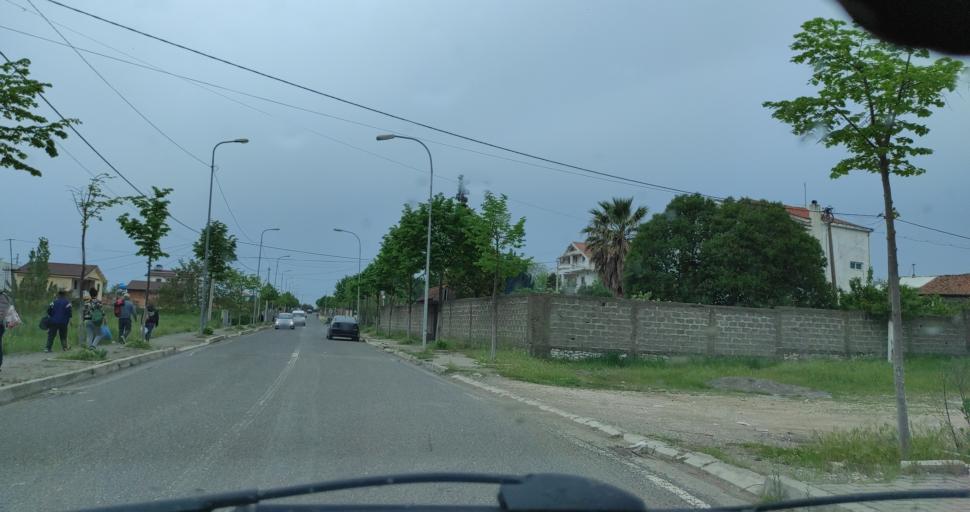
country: AL
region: Lezhe
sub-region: Rrethi i Kurbinit
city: Mamurras
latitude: 41.5842
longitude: 19.6932
